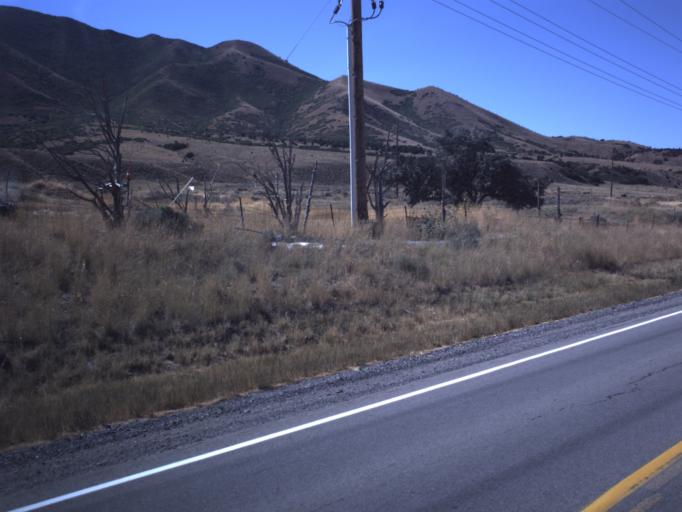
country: US
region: Utah
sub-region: Tooele County
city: Tooele
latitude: 40.4931
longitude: -112.3317
